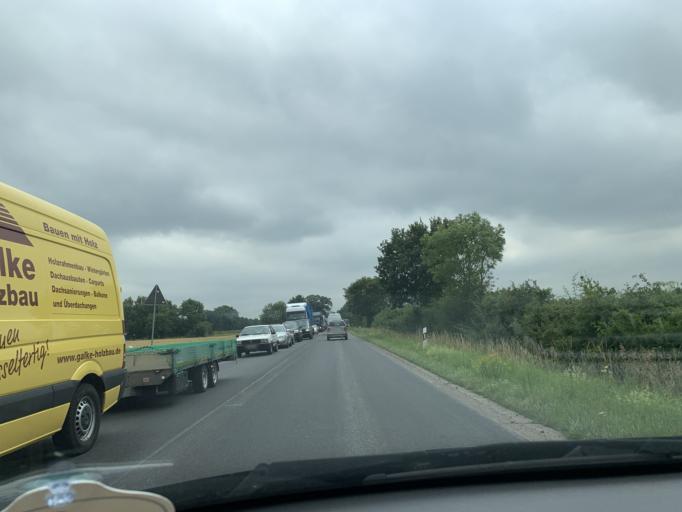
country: DE
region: North Rhine-Westphalia
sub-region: Regierungsbezirk Munster
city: Ennigerloh
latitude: 51.8946
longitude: 8.0512
